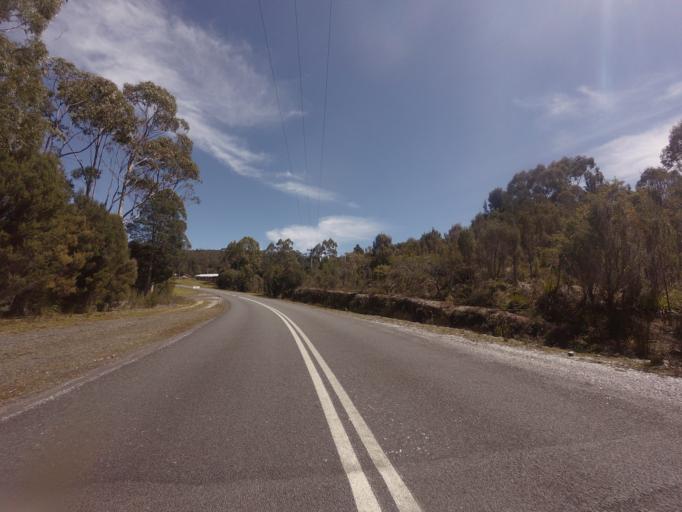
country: AU
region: Tasmania
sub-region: West Coast
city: Queenstown
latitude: -42.7655
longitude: 146.0471
